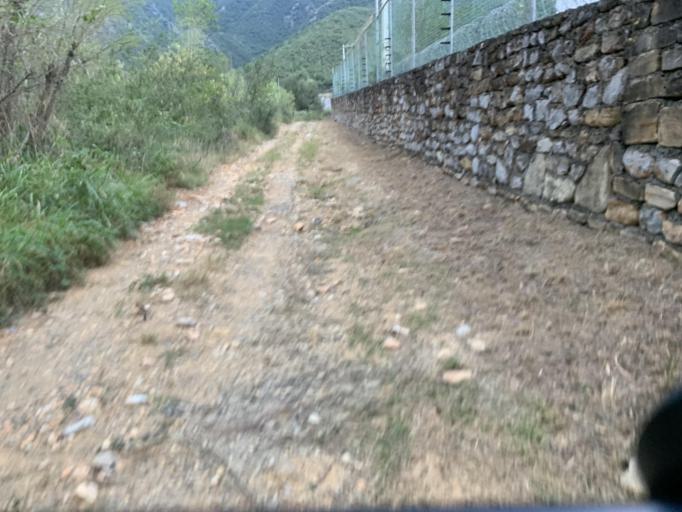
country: MX
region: Nuevo Leon
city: Santiago
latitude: 25.5044
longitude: -100.1804
